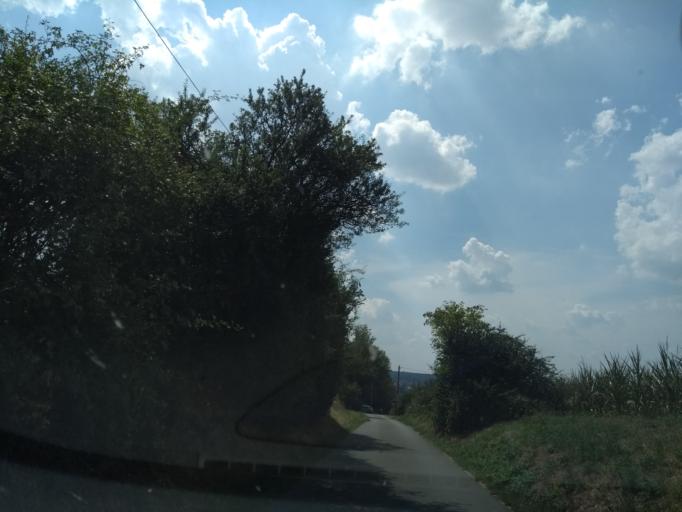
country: DE
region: Thuringia
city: Eisenberg
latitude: 50.9777
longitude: 11.9057
